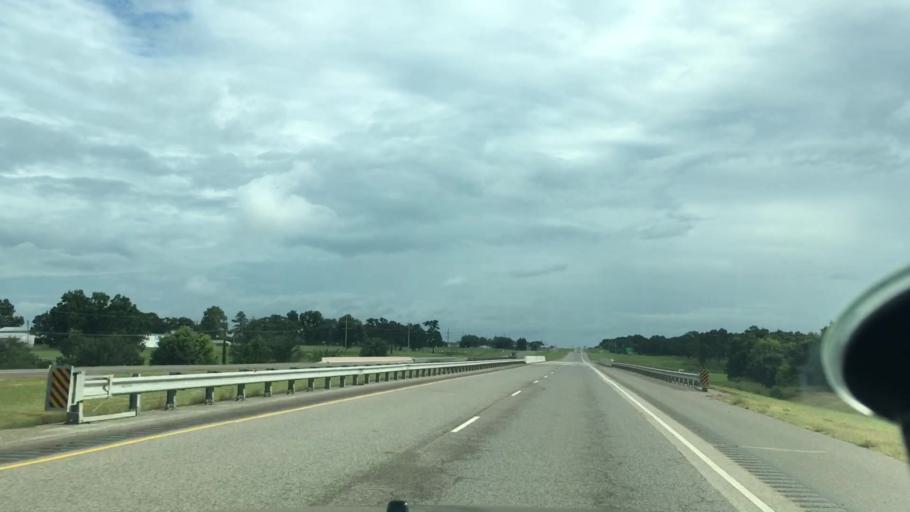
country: US
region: Oklahoma
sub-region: Lincoln County
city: Prague
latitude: 35.3618
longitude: -96.6718
